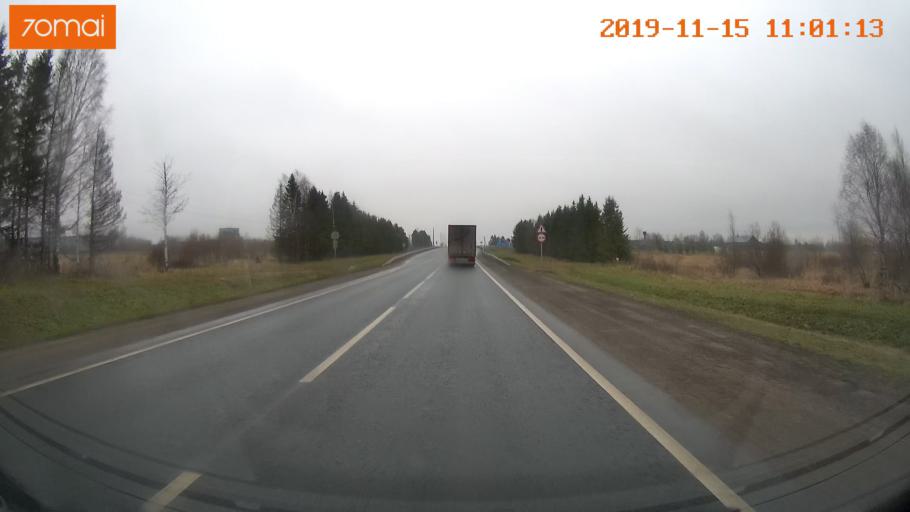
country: RU
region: Vologda
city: Chebsara
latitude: 59.1338
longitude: 38.9156
